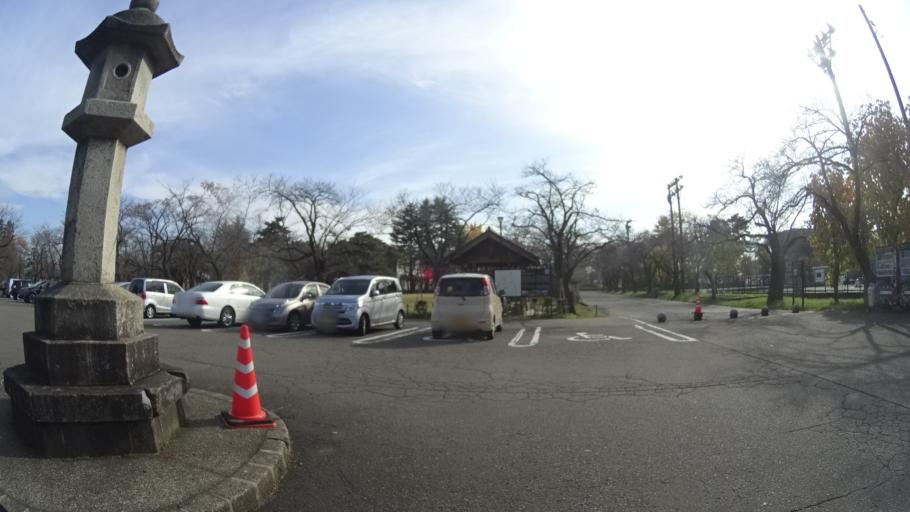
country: JP
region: Niigata
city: Joetsu
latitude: 37.1089
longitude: 138.2551
